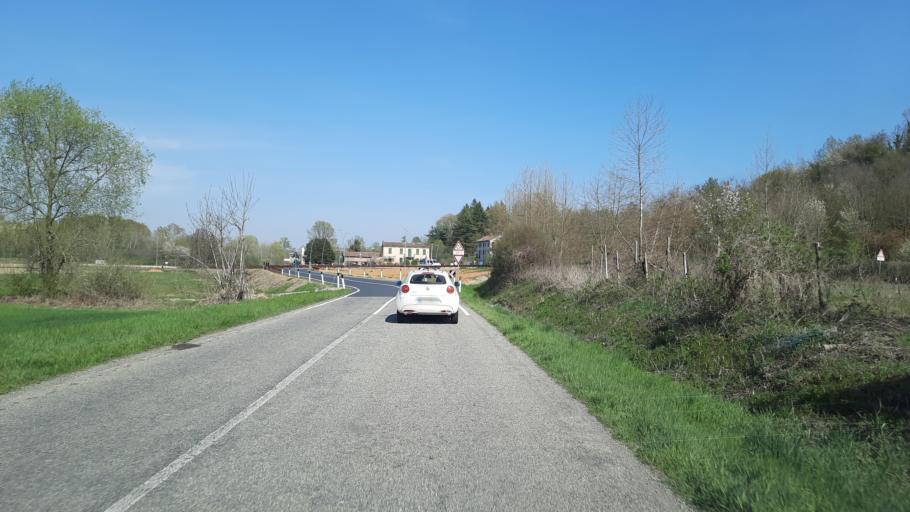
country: IT
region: Piedmont
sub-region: Provincia di Alessandria
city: Vignale Monferrato
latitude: 45.0194
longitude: 8.3887
